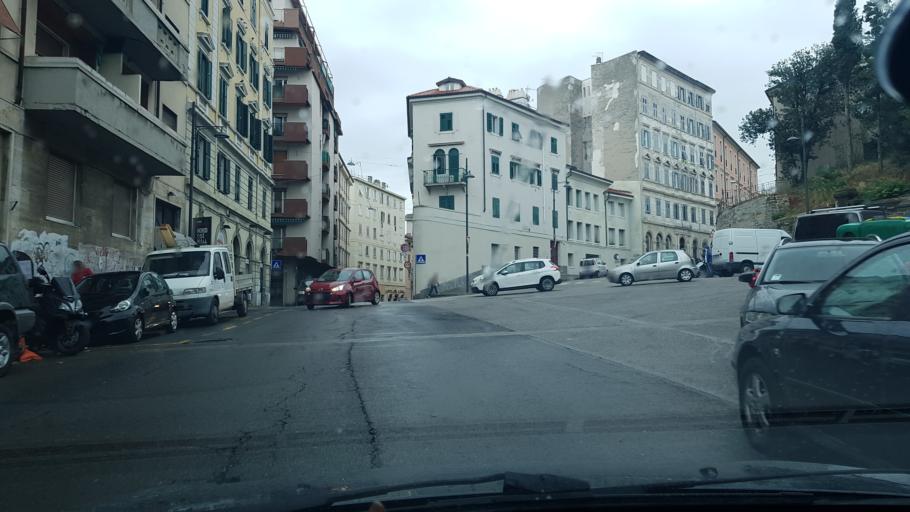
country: IT
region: Friuli Venezia Giulia
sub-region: Provincia di Trieste
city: Trieste
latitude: 45.6446
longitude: 13.7771
